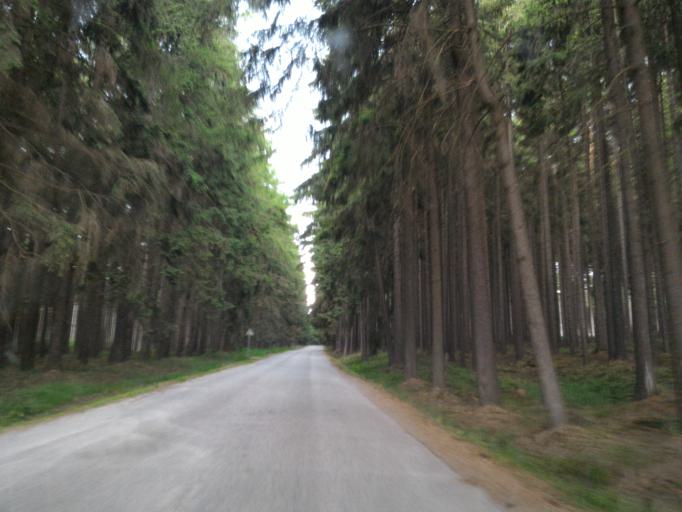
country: CZ
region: Vysocina
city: Zeletava
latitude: 49.1278
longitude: 15.5852
